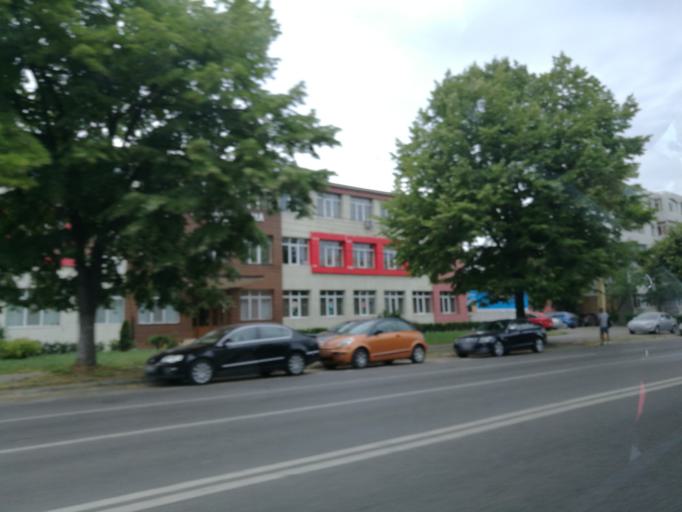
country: RO
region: Constanta
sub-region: Municipiul Constanta
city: Constanta
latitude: 44.1926
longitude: 28.6330
